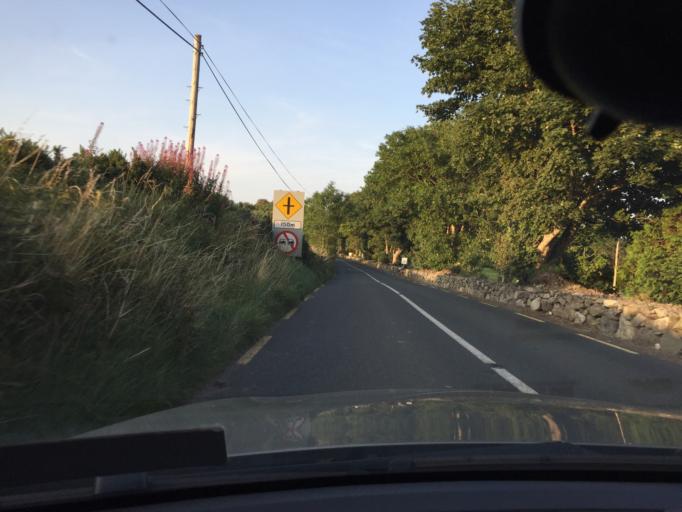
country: IE
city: Newtownmountkennedy
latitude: 53.1025
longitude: -6.1974
